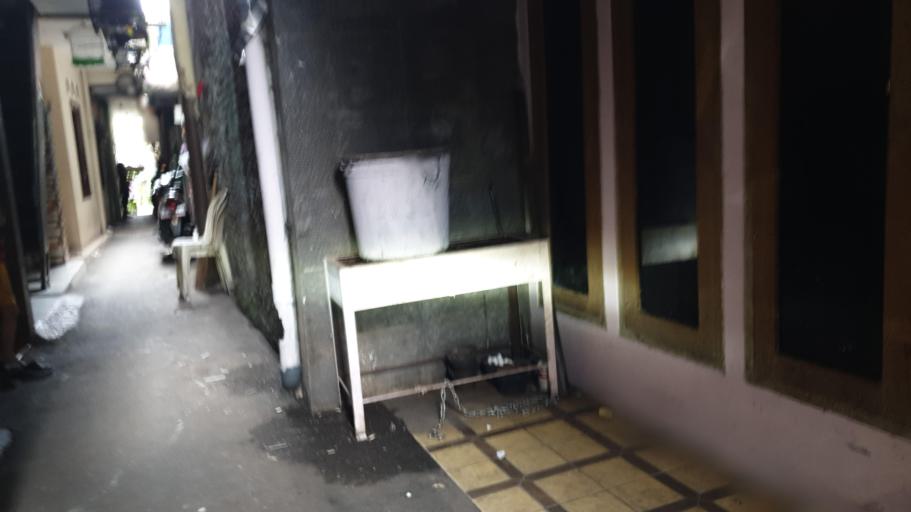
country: ID
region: Banten
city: South Tangerang
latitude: -6.2665
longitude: 106.7888
